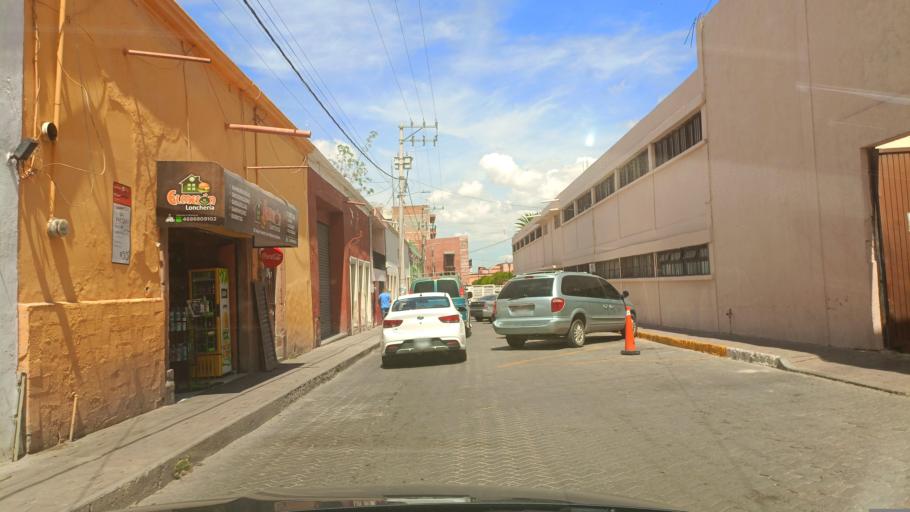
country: MX
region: Guanajuato
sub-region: San Luis de la Paz
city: San Luis de la Paz
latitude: 21.2980
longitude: -100.5136
